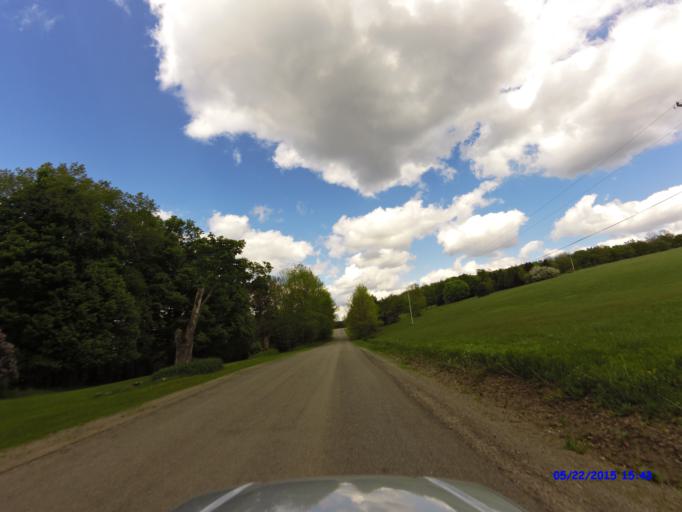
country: US
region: New York
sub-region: Cattaraugus County
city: Franklinville
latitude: 42.3129
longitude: -78.5708
